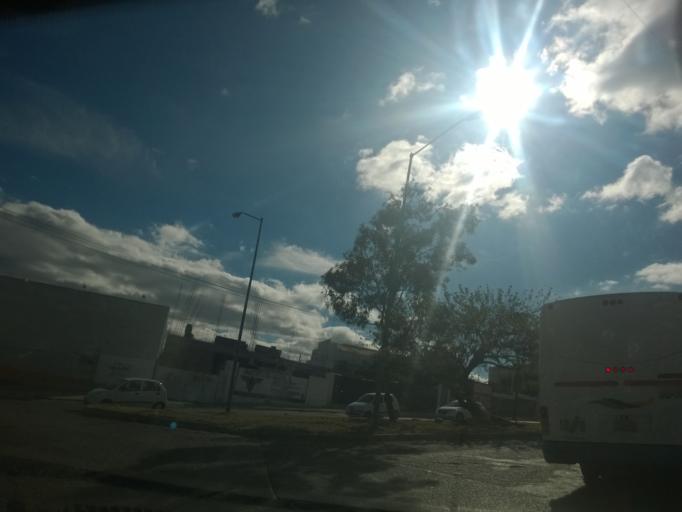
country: MX
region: Guanajuato
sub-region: Leon
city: Ejido la Joya
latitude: 21.1217
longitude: -101.7217
